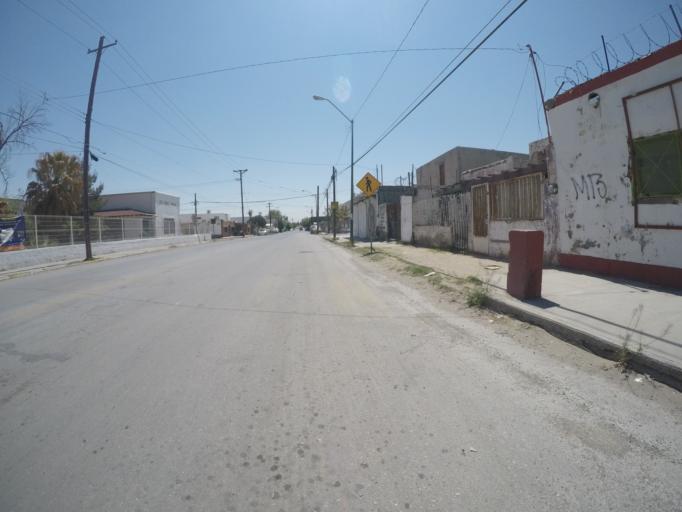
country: MX
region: Chihuahua
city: Ciudad Juarez
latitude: 31.7266
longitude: -106.4832
